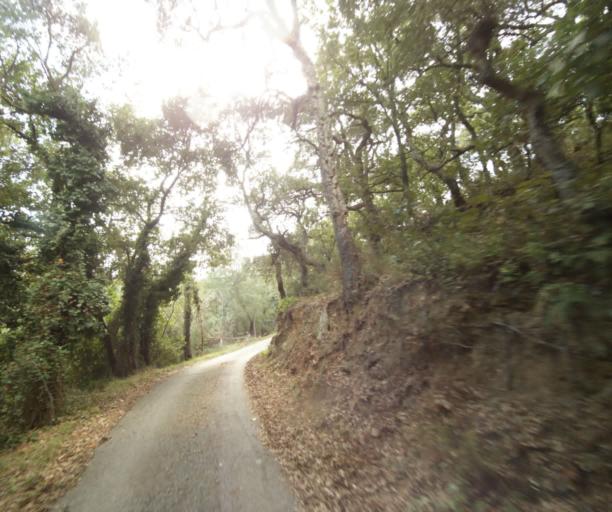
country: FR
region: Languedoc-Roussillon
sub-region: Departement des Pyrenees-Orientales
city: Argelers
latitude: 42.5306
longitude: 3.0168
